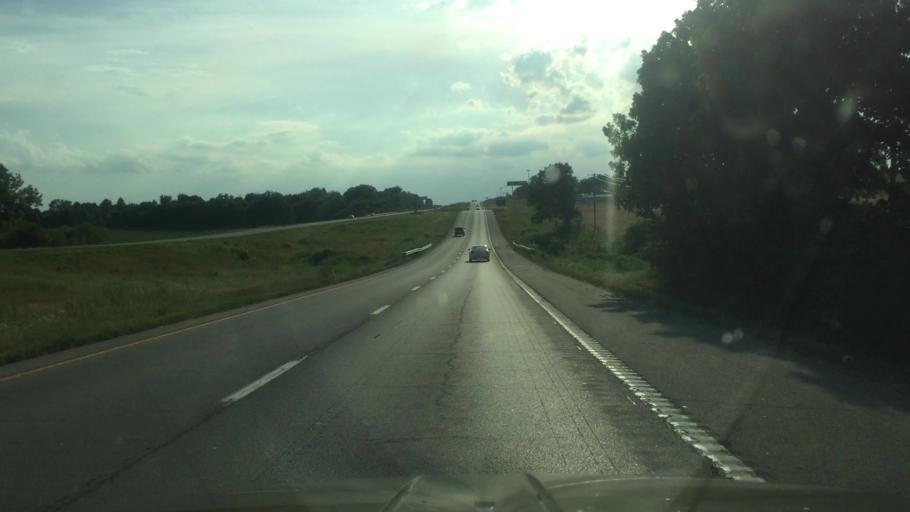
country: US
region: Missouri
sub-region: Jackson County
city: Lone Jack
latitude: 38.8694
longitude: -94.1009
